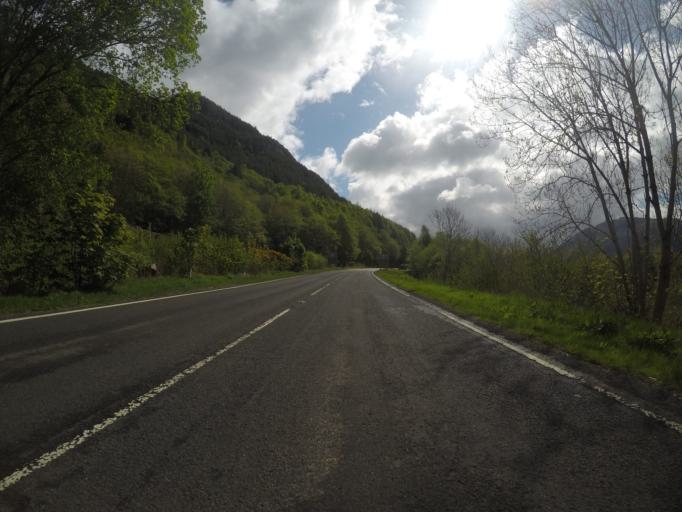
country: GB
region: Scotland
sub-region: Highland
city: Fort William
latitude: 57.2472
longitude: -5.4663
